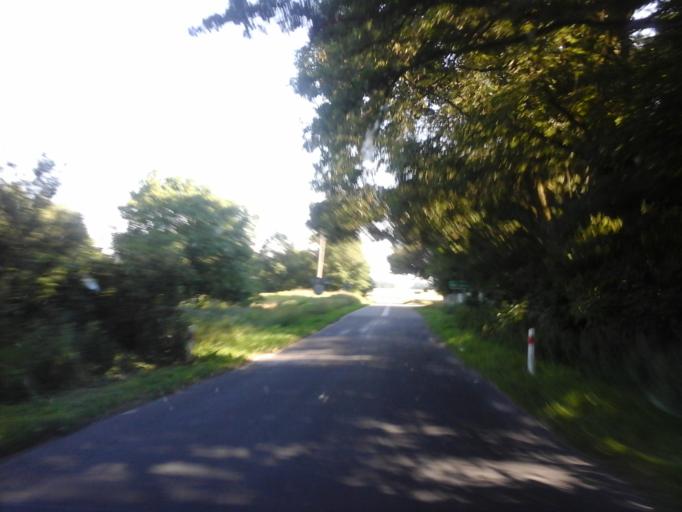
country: PL
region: West Pomeranian Voivodeship
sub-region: Powiat lobeski
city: Dobra
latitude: 53.5286
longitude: 15.3145
